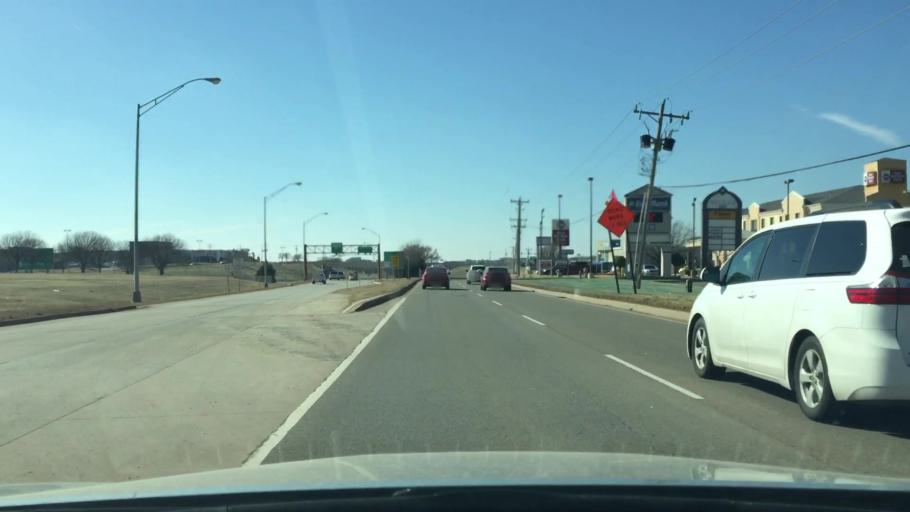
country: US
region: Oklahoma
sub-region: Oklahoma County
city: The Village
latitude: 35.6091
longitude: -97.5336
